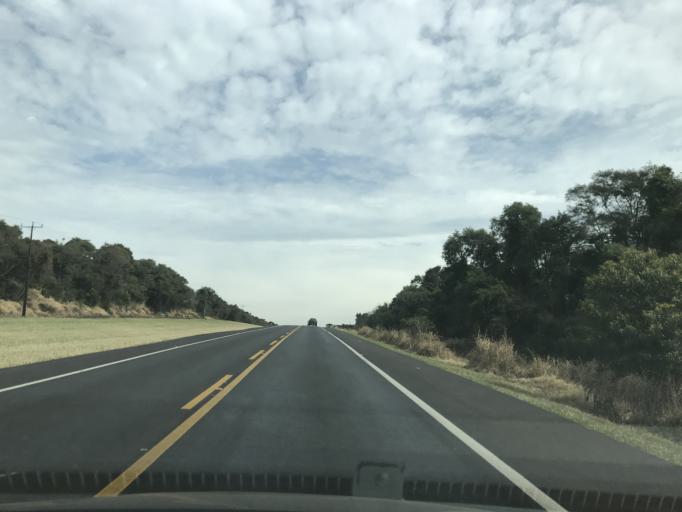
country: BR
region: Parana
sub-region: Cascavel
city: Cascavel
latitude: -25.0634
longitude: -53.6513
